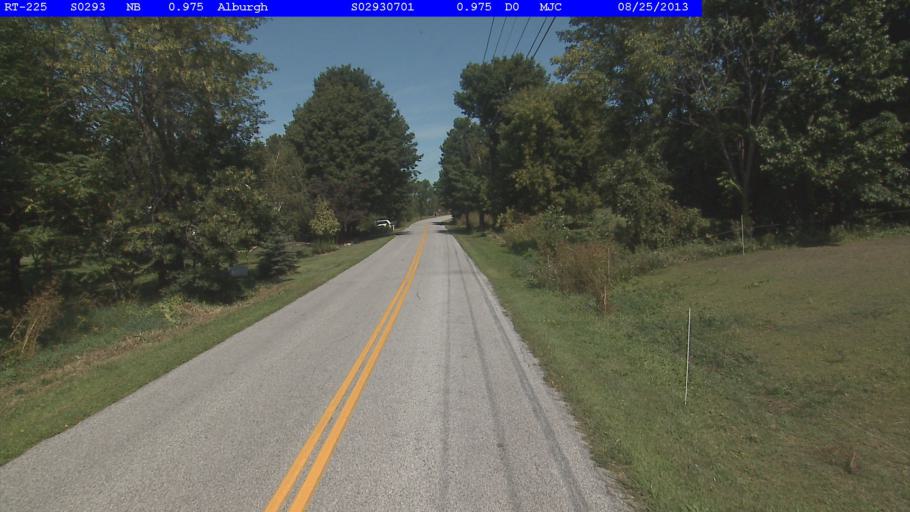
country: US
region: New York
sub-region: Clinton County
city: Rouses Point
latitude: 45.0027
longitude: -73.2958
